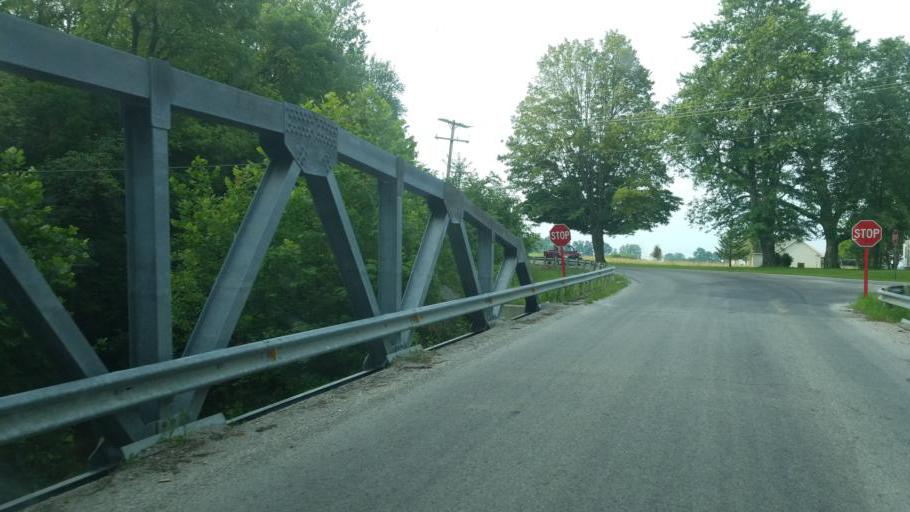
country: US
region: Ohio
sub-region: Morrow County
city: Mount Gilead
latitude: 40.5454
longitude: -82.8541
